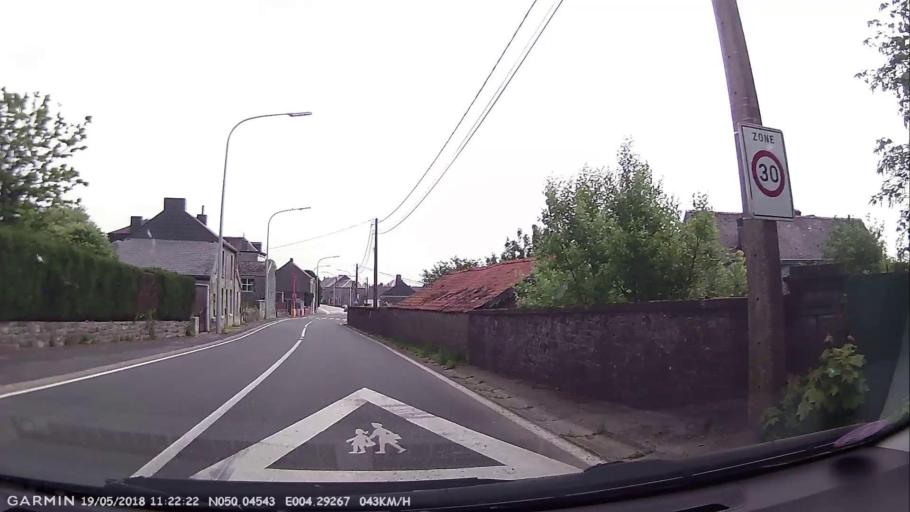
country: BE
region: Wallonia
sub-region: Province du Hainaut
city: Chimay
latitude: 50.0455
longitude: 4.2929
